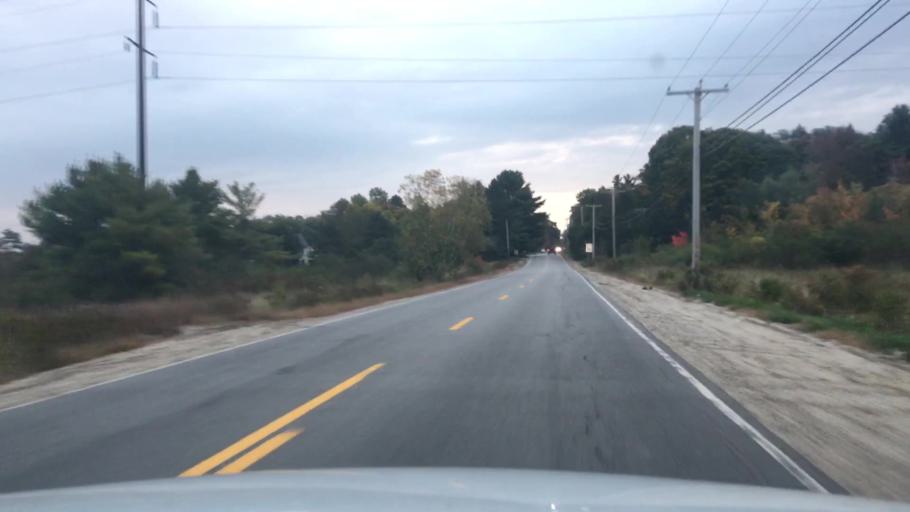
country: US
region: Maine
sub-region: York County
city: Buxton
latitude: 43.6394
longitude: -70.5228
